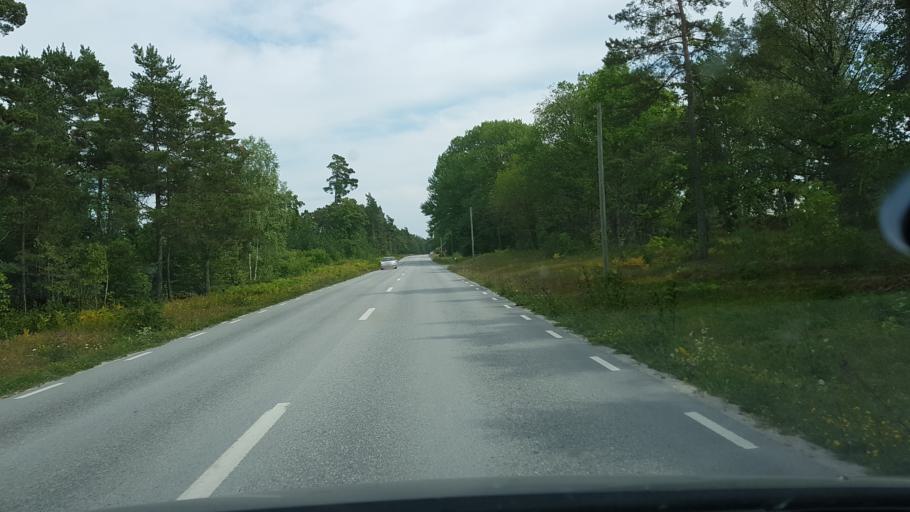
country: SE
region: Gotland
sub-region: Gotland
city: Slite
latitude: 57.7464
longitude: 18.6725
